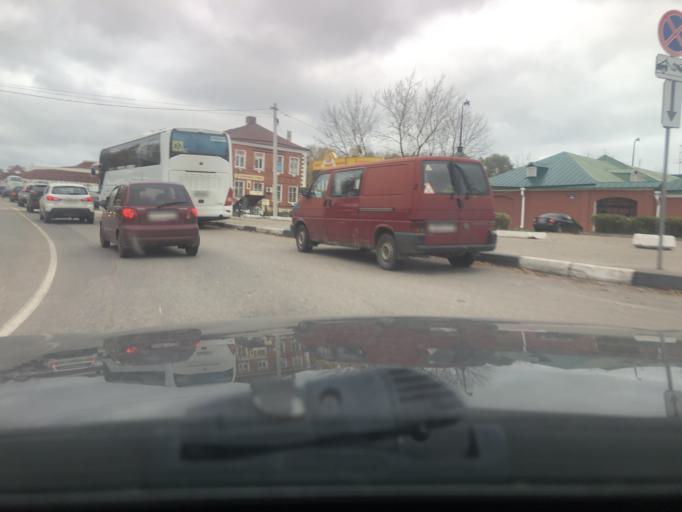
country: RU
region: Moskovskaya
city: Sergiyev Posad
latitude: 56.3136
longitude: 38.1314
